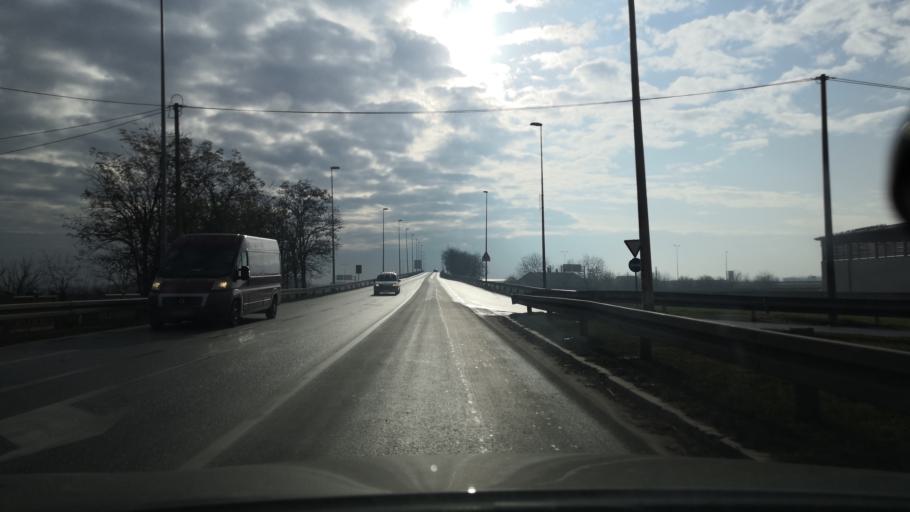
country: RS
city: Dobanovci
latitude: 44.8469
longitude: 20.2097
